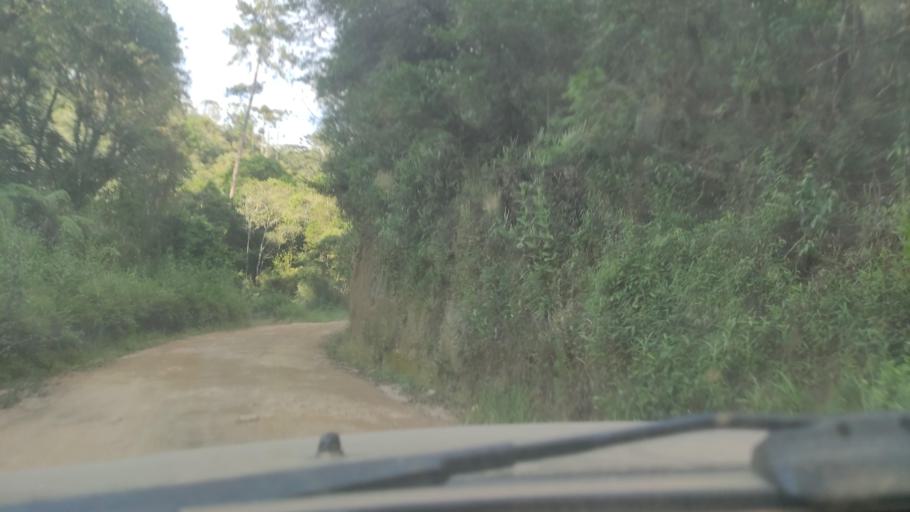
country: BR
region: Minas Gerais
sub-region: Cambui
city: Cambui
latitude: -22.7521
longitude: -45.9332
